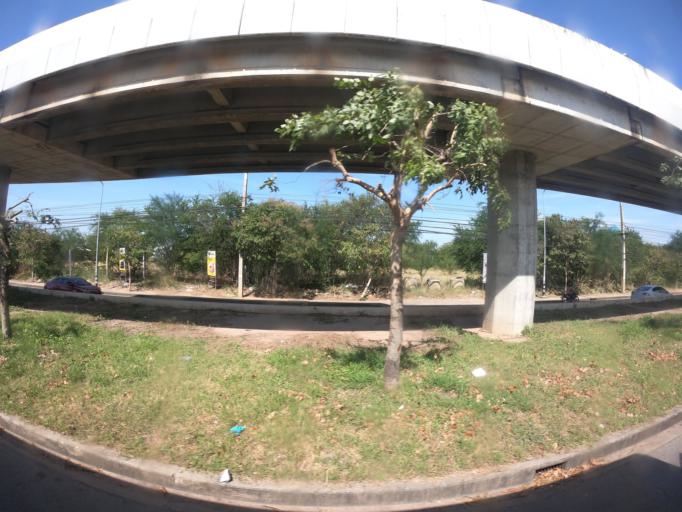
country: TH
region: Nakhon Ratchasima
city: Nakhon Ratchasima
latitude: 15.0043
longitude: 102.1211
